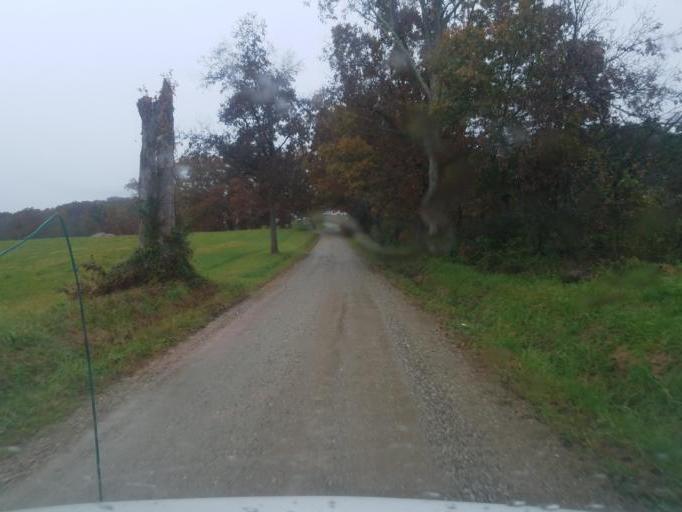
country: US
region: Ohio
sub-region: Washington County
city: Beverly
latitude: 39.4696
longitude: -81.6584
